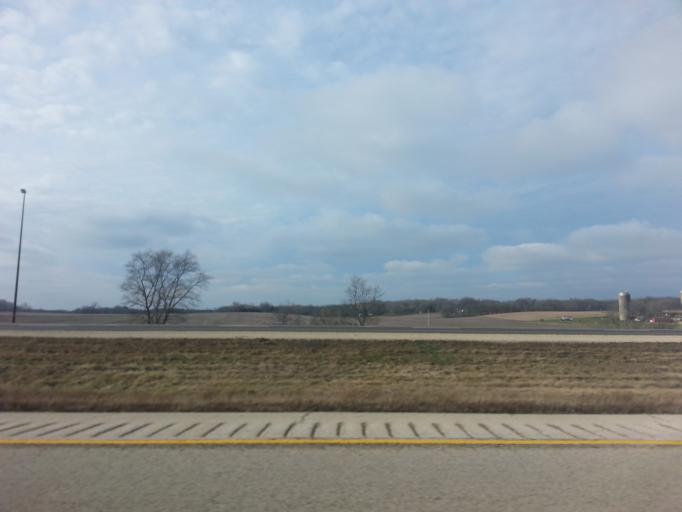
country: US
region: Illinois
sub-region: Ogle County
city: Davis Junction
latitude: 42.1704
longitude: -89.0235
